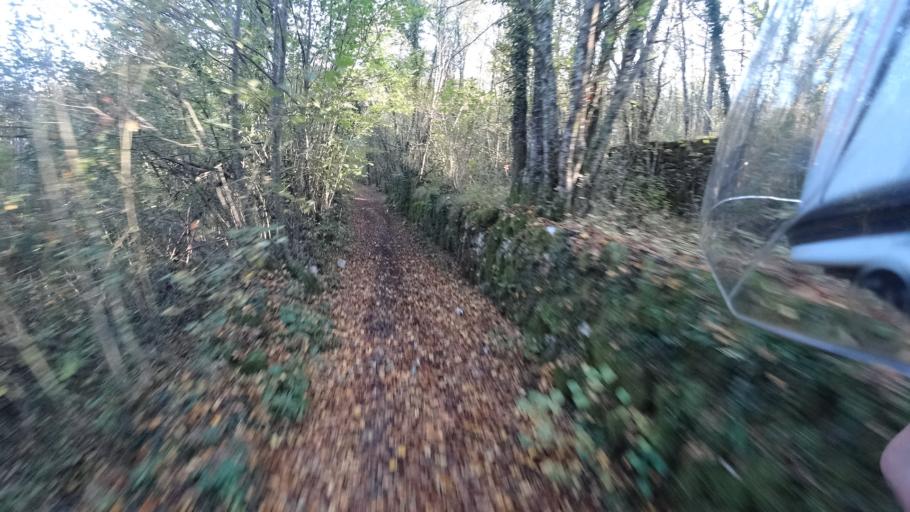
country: HR
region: Primorsko-Goranska
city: Matulji
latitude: 45.4046
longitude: 14.2874
